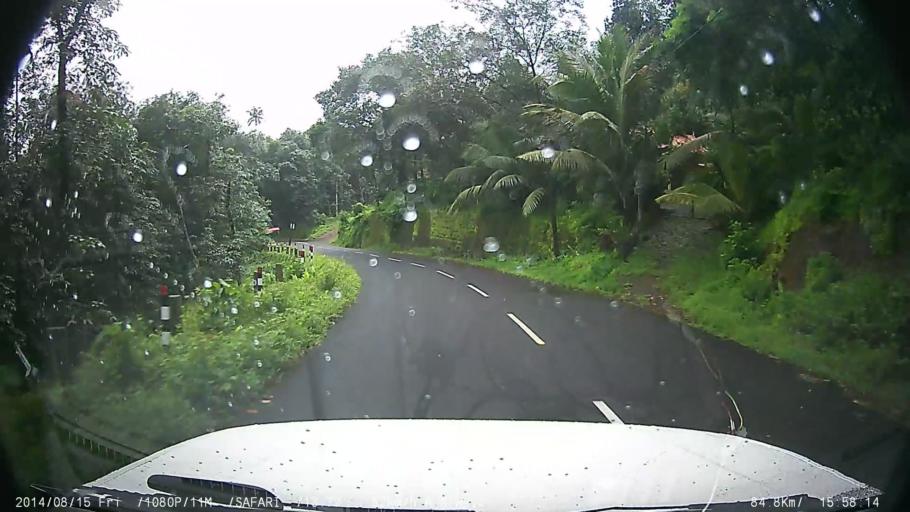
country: IN
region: Kerala
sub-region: Kottayam
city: Lalam
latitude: 9.7798
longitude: 76.7256
